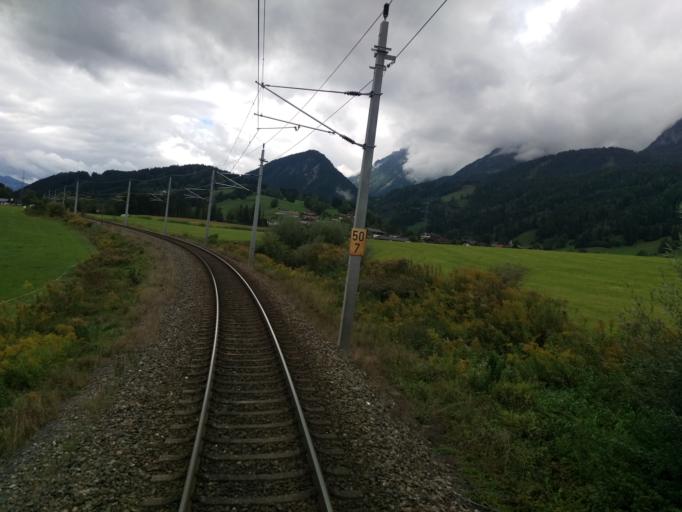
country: AT
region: Styria
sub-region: Politischer Bezirk Liezen
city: Haus im Ennstal
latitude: 47.4215
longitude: 13.7896
